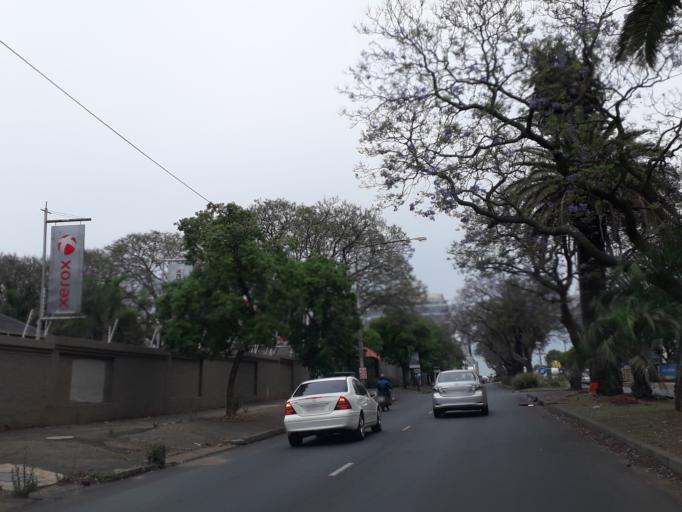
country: ZA
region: Gauteng
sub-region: City of Johannesburg Metropolitan Municipality
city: Johannesburg
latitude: -26.1521
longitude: 28.0454
